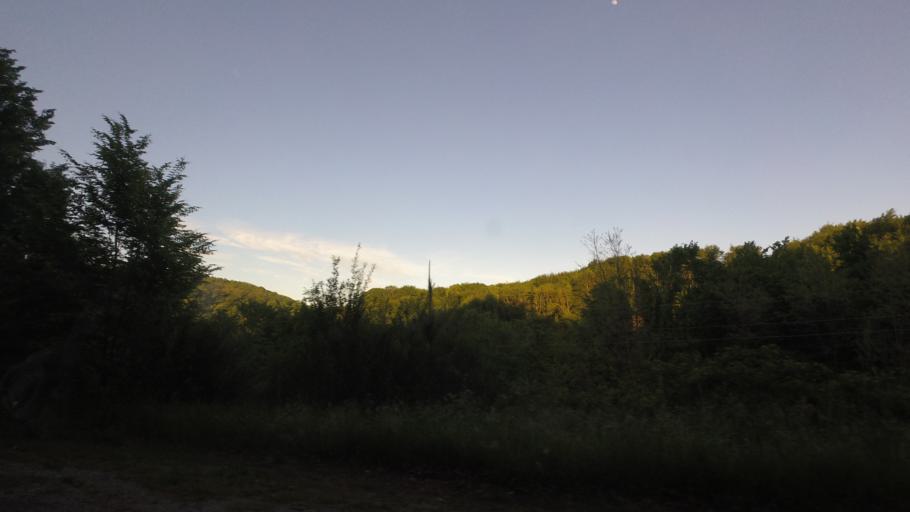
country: HR
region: Karlovacka
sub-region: Grad Karlovac
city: Karlovac
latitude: 45.4033
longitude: 15.5639
